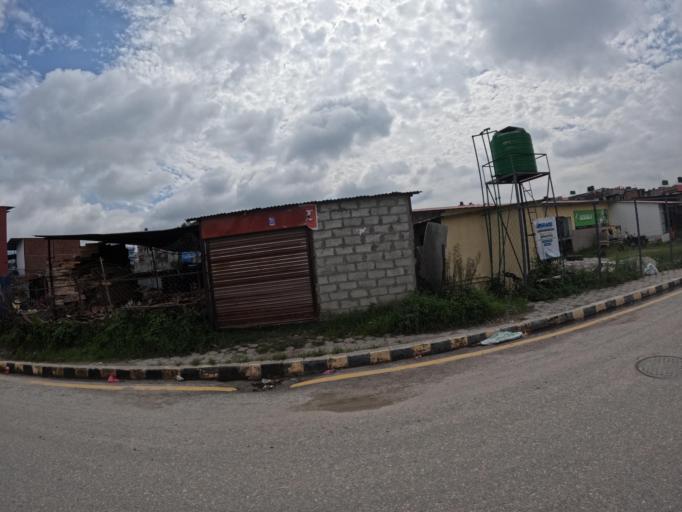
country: NP
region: Central Region
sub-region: Bagmati Zone
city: Kathmandu
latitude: 27.7598
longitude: 85.3163
